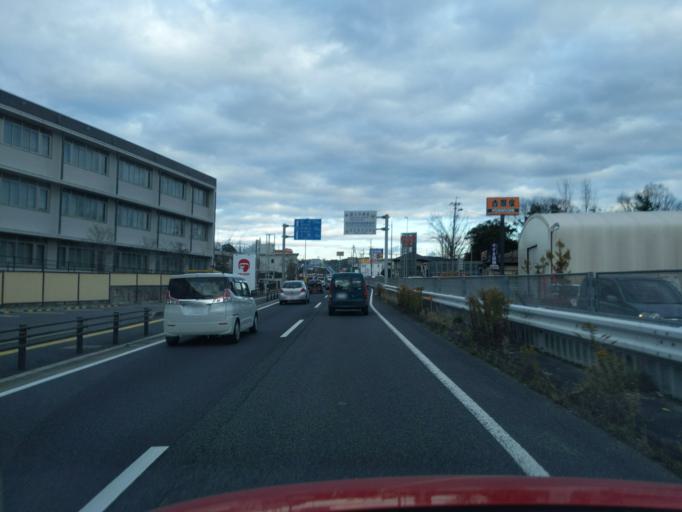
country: JP
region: Gifu
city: Tajimi
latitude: 35.3408
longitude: 137.1301
